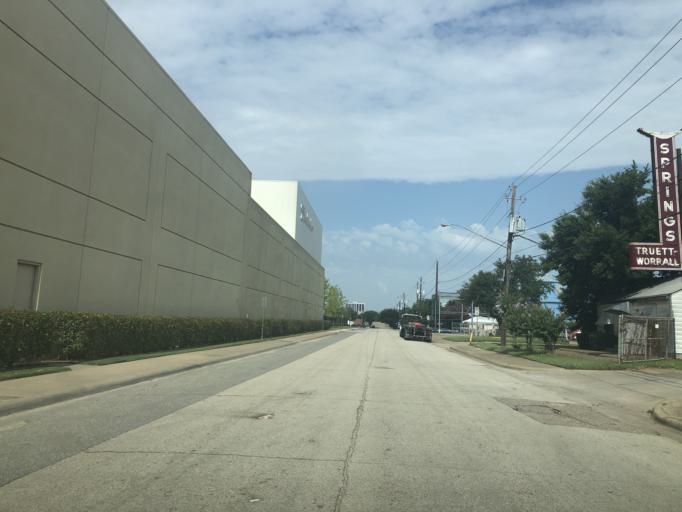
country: US
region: Texas
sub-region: Dallas County
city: Dallas
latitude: 32.8193
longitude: -96.8525
